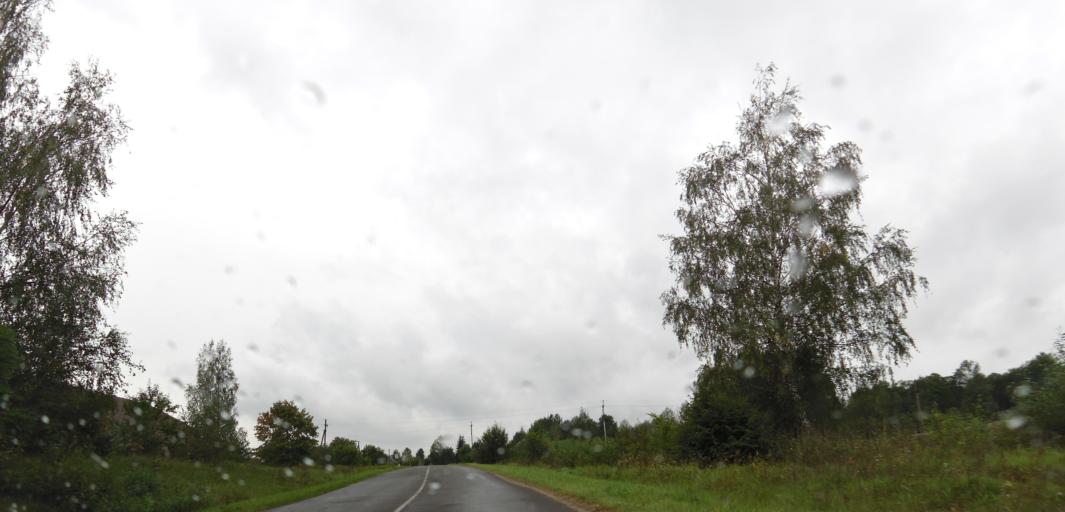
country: LT
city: Sirvintos
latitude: 55.0741
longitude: 25.0586
